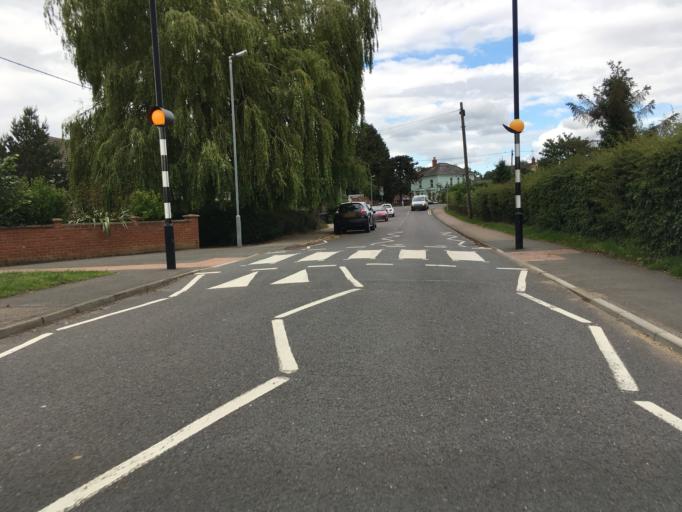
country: GB
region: England
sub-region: Central Bedfordshire
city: Leighton Buzzard
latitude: 51.9452
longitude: -0.6588
